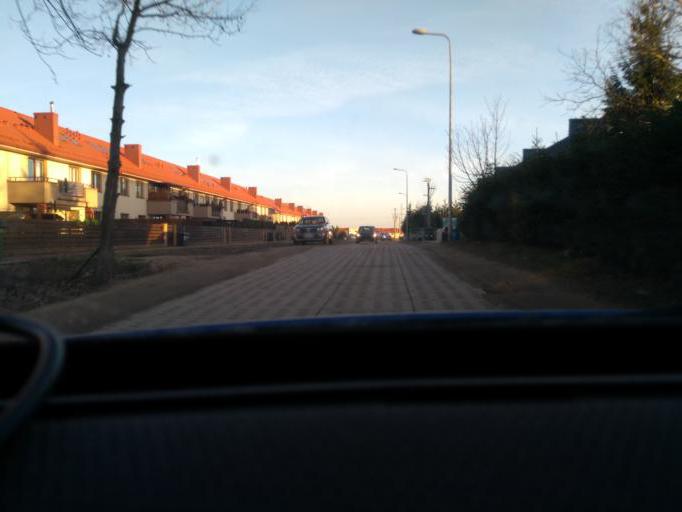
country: PL
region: Pomeranian Voivodeship
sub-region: Powiat kartuski
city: Banino
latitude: 54.3876
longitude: 18.3834
